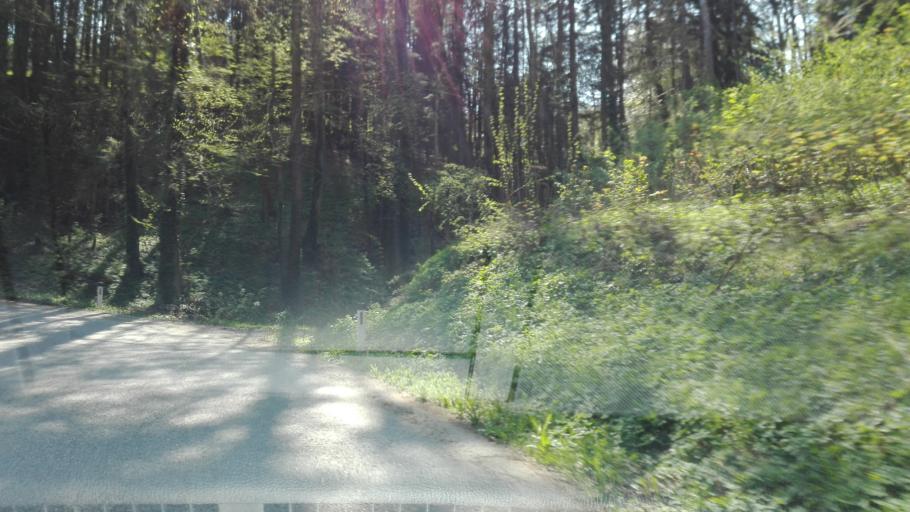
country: AT
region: Upper Austria
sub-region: Politischer Bezirk Rohrbach
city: Atzesberg
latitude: 48.4282
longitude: 13.9196
